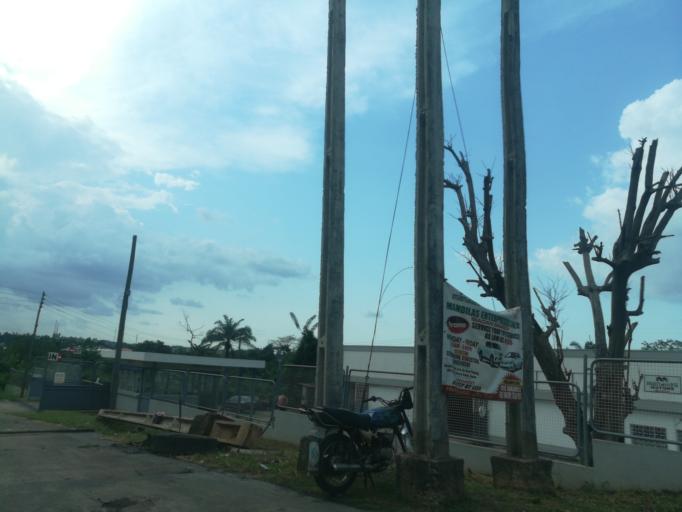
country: NG
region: Oyo
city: Ibadan
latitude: 7.3676
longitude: 3.8523
